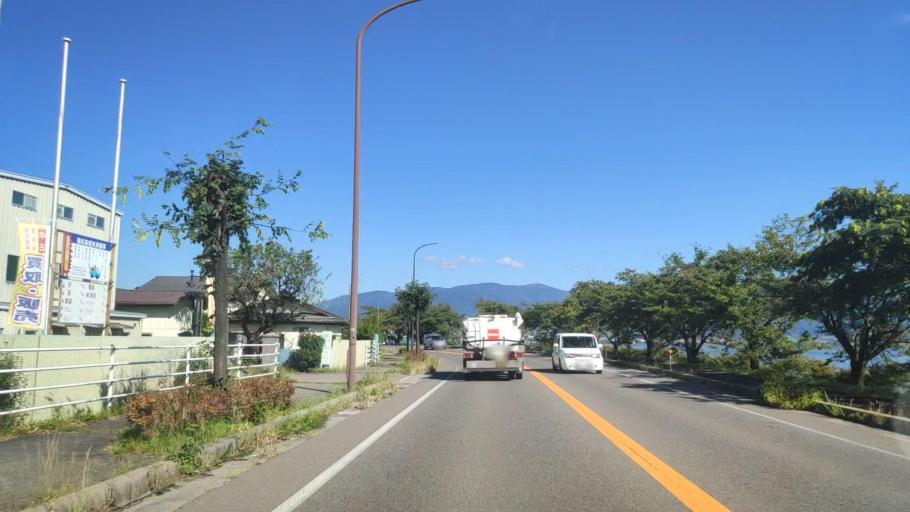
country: JP
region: Nagano
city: Okaya
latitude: 36.0360
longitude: 138.0697
